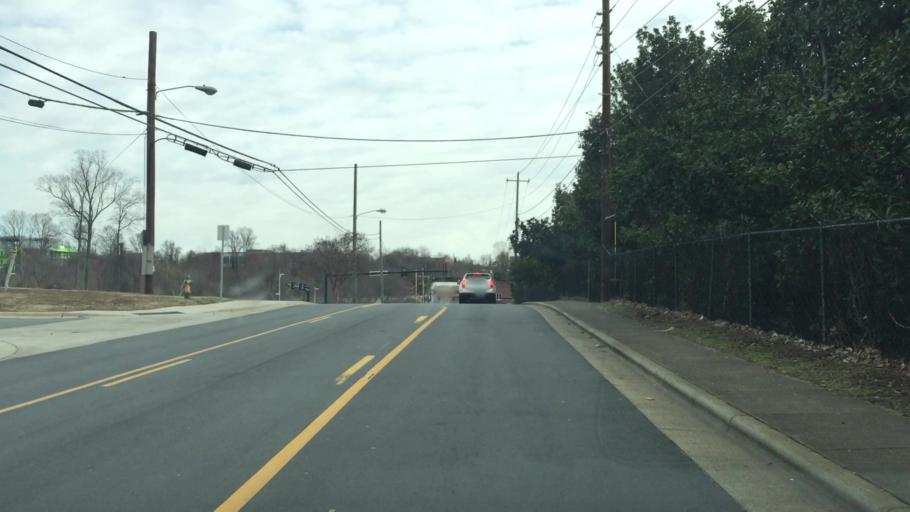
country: US
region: North Carolina
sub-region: Forsyth County
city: Winston-Salem
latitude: 36.0898
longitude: -80.2350
